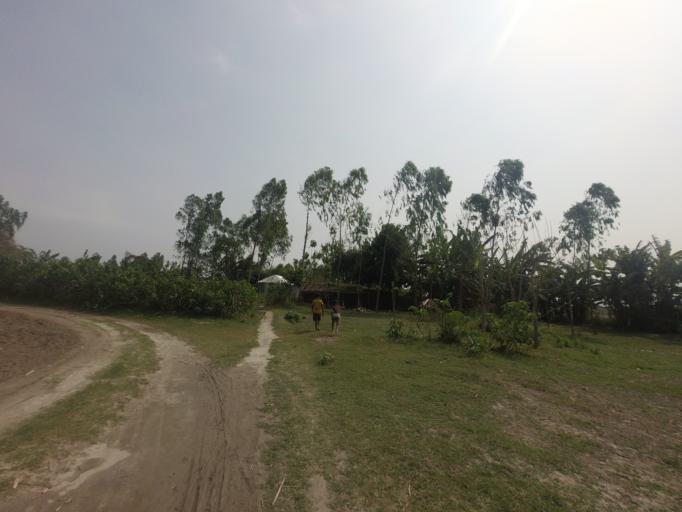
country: BD
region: Rajshahi
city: Sirajganj
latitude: 24.3485
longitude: 89.7283
